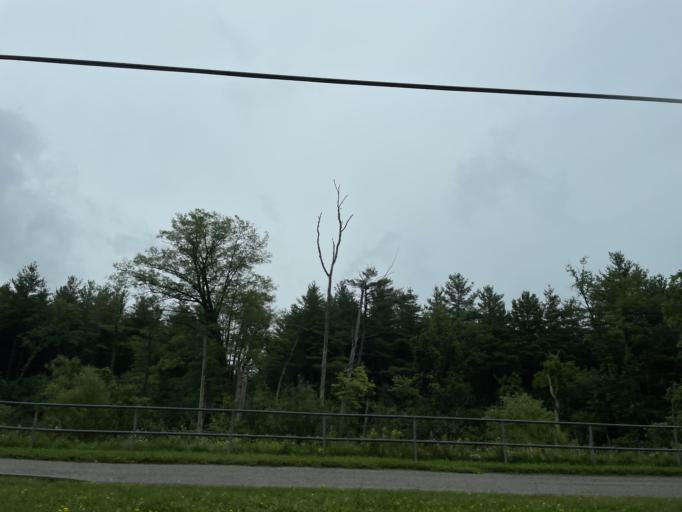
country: CA
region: Ontario
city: Cambridge
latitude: 43.4133
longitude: -80.2800
